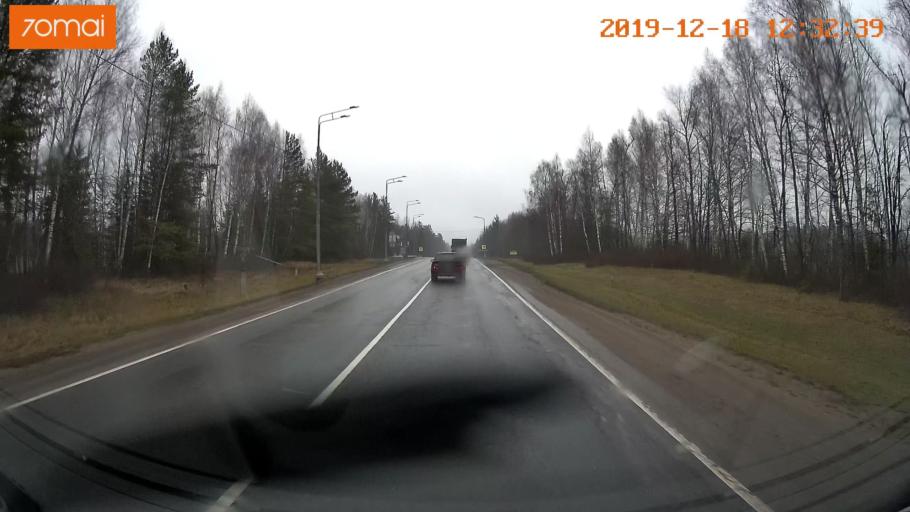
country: RU
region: Moskovskaya
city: Rumyantsevo
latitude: 56.1070
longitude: 36.5530
